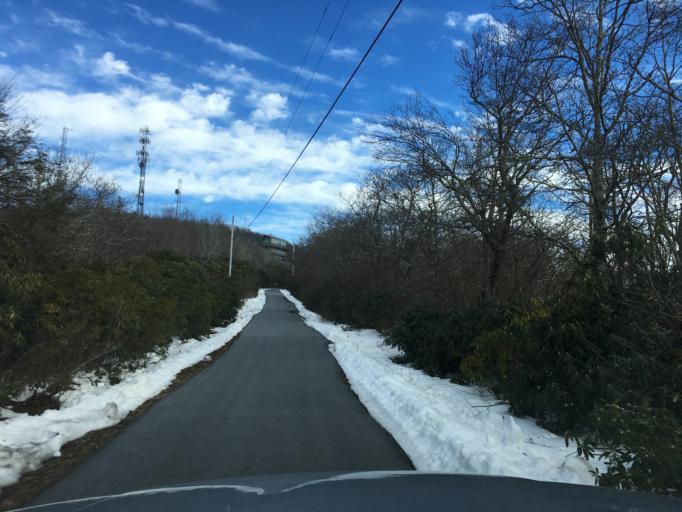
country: US
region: North Carolina
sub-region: Jackson County
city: Cullowhee
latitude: 35.1320
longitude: -82.9865
